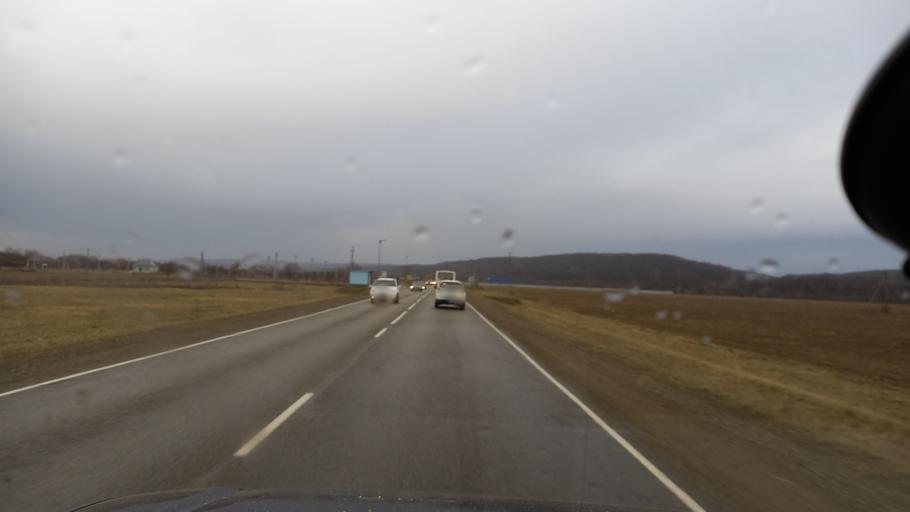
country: RU
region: Adygeya
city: Tul'skiy
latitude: 44.5334
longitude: 40.1387
